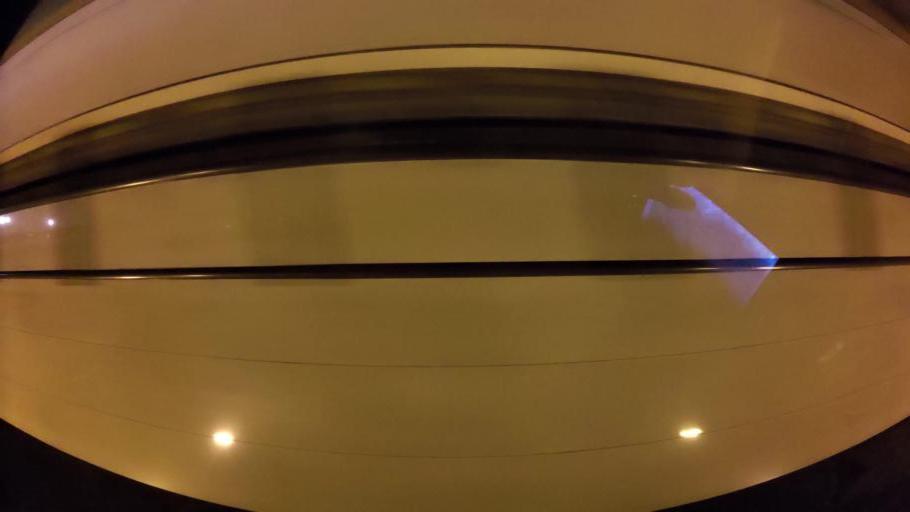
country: EC
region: Pichincha
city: Quito
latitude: -0.2168
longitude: -78.5185
